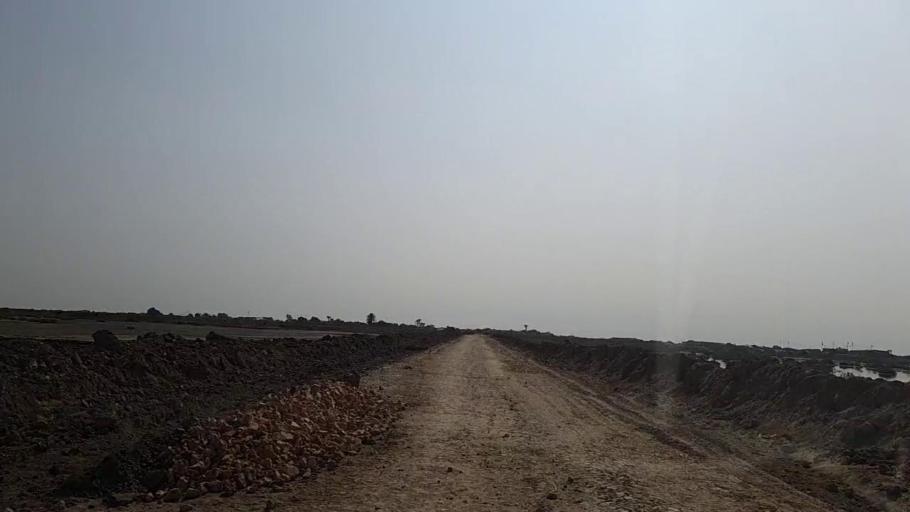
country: PK
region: Sindh
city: Chuhar Jamali
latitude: 24.1949
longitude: 67.8482
